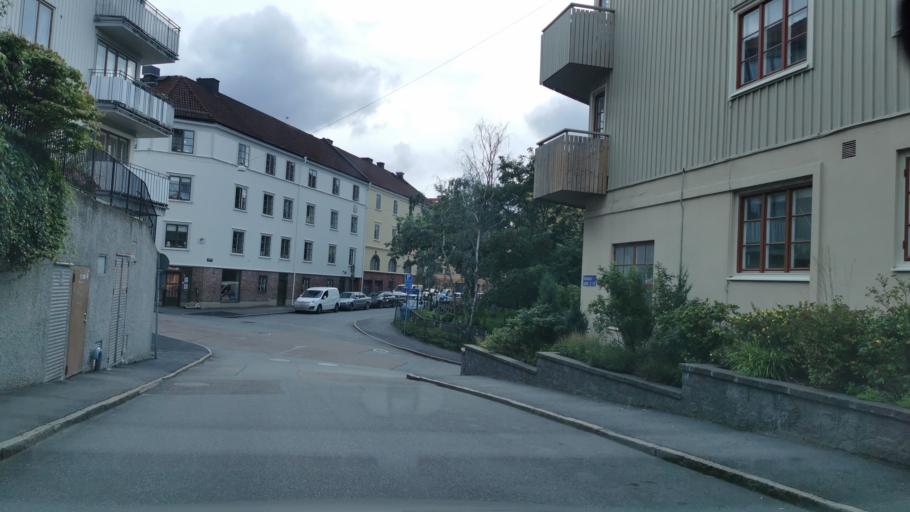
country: SE
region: Vaestra Goetaland
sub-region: Goteborg
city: Goeteborg
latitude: 57.6950
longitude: 11.9443
